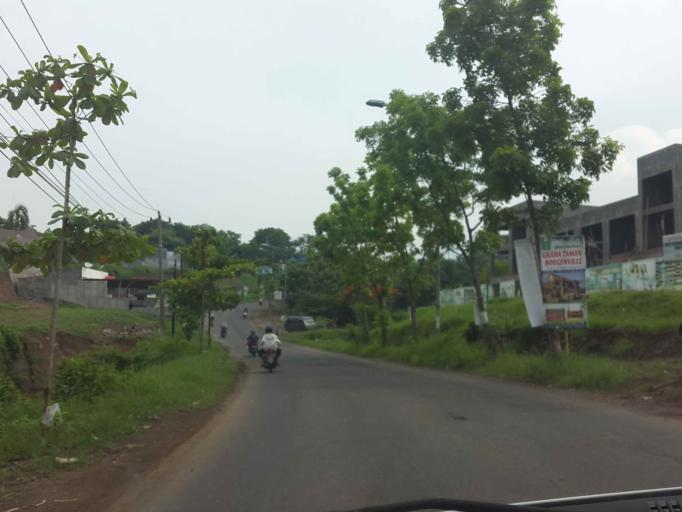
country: ID
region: Central Java
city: Mranggen
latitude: -7.0394
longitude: 110.4591
